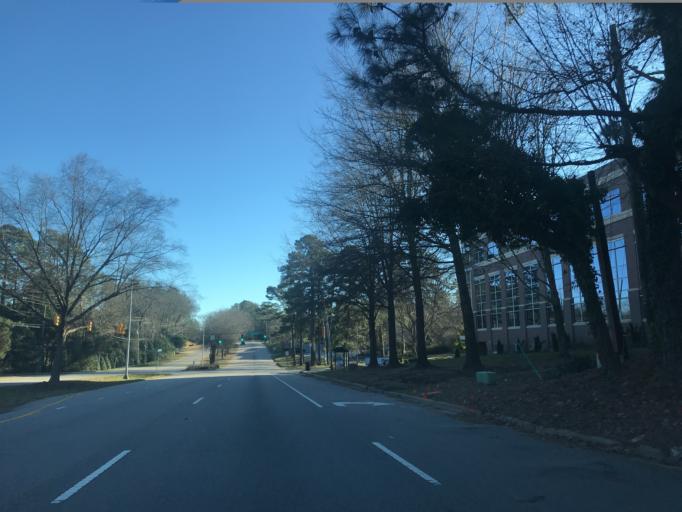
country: US
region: North Carolina
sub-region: Wake County
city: West Raleigh
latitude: 35.8271
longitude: -78.6663
